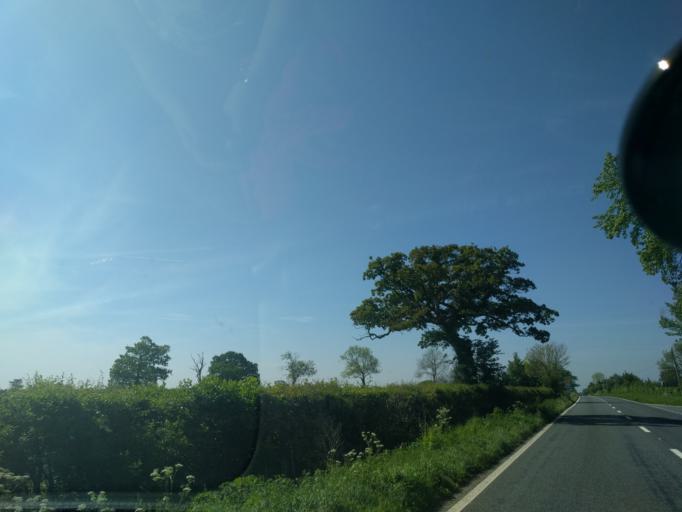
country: GB
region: England
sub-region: Somerset
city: Castle Cary
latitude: 51.1043
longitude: -2.5925
